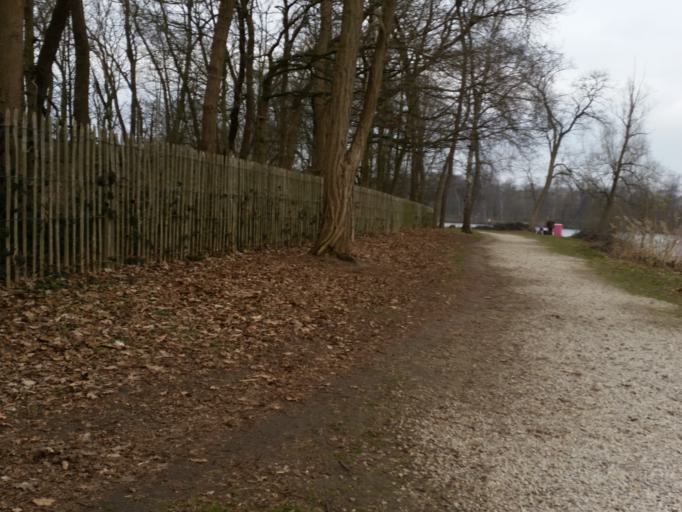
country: BE
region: Flanders
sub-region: Provincie Vlaams-Brabant
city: Zemst
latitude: 50.9858
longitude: 4.5055
